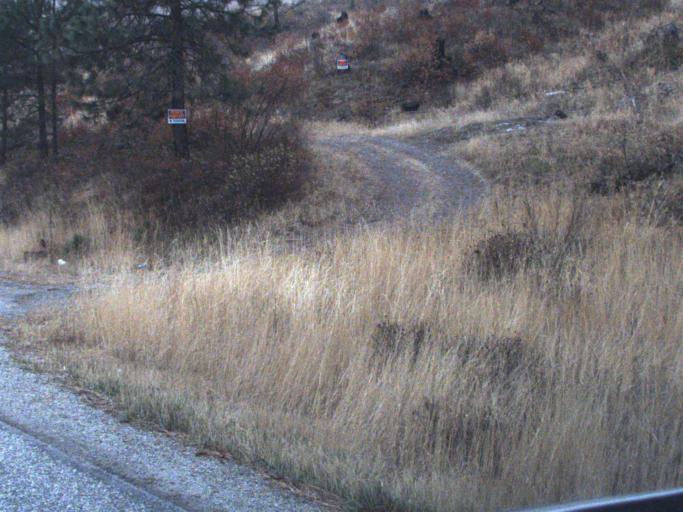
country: US
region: Washington
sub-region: Stevens County
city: Kettle Falls
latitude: 48.7572
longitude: -118.1359
